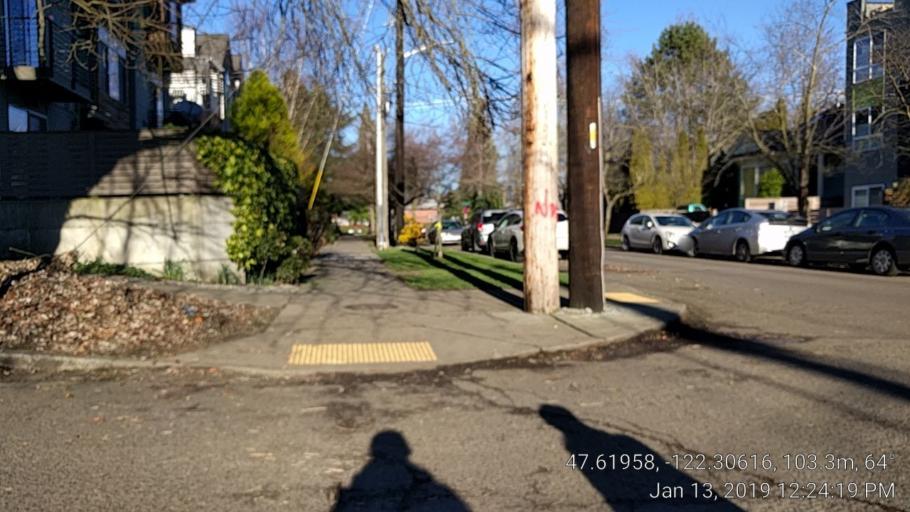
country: US
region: Washington
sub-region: King County
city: Seattle
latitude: 47.6196
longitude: -122.3061
